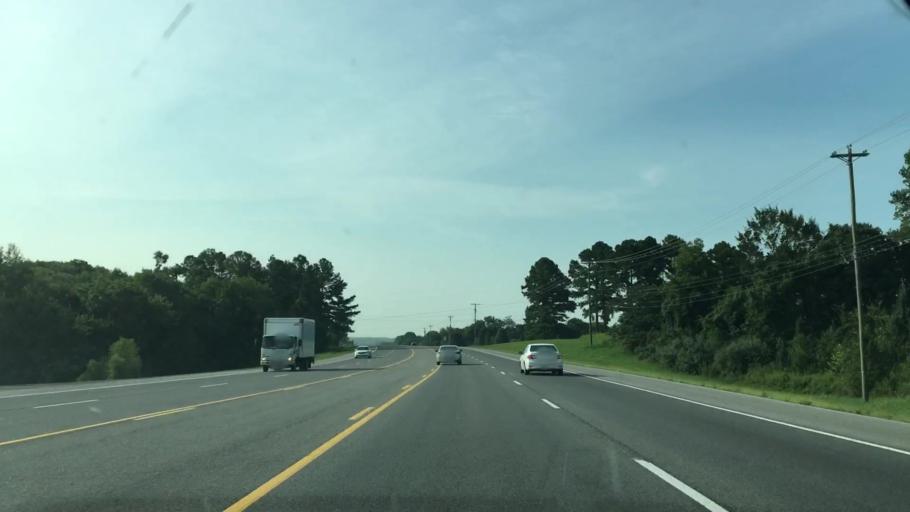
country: US
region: Tennessee
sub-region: Wilson County
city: Mount Juliet
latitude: 36.2090
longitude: -86.4200
